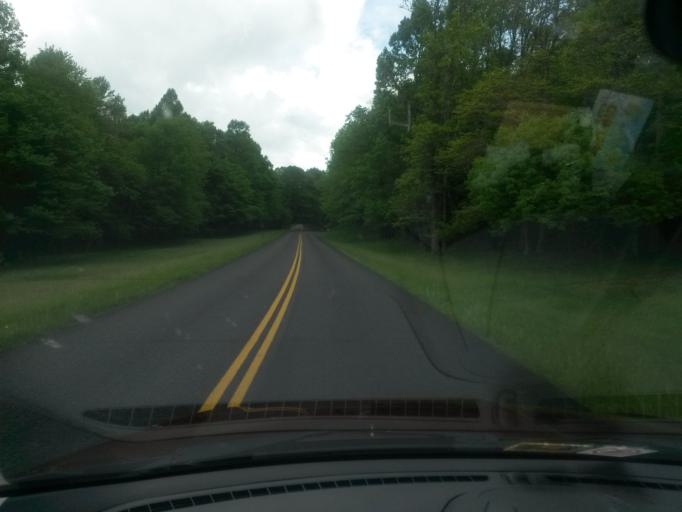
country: US
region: Virginia
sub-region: Floyd County
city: Floyd
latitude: 36.8134
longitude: -80.3457
